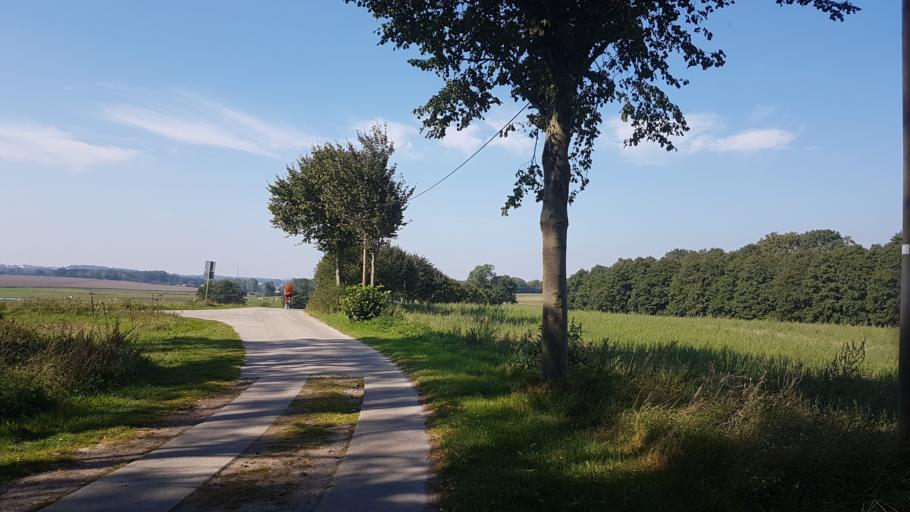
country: DE
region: Mecklenburg-Vorpommern
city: Putbus
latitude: 54.3499
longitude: 13.5322
